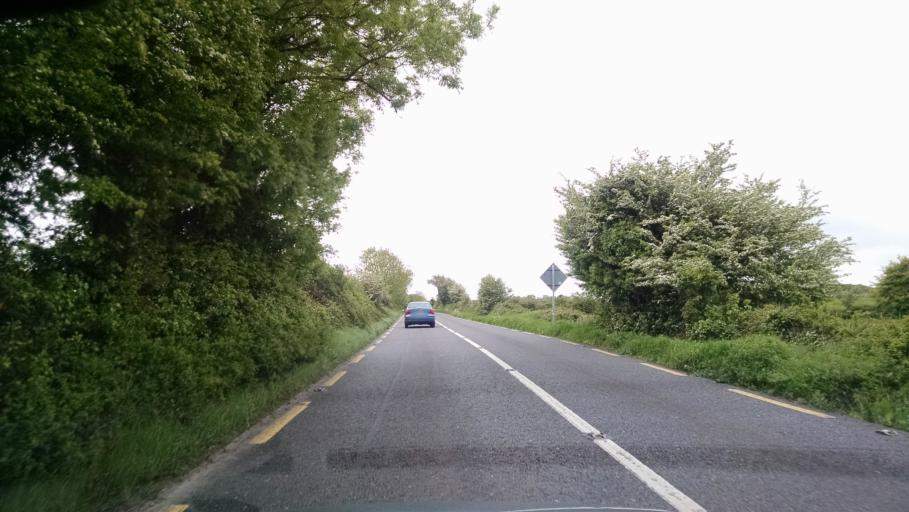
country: IE
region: Connaught
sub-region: County Galway
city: Claregalway
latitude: 53.4028
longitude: -9.0171
